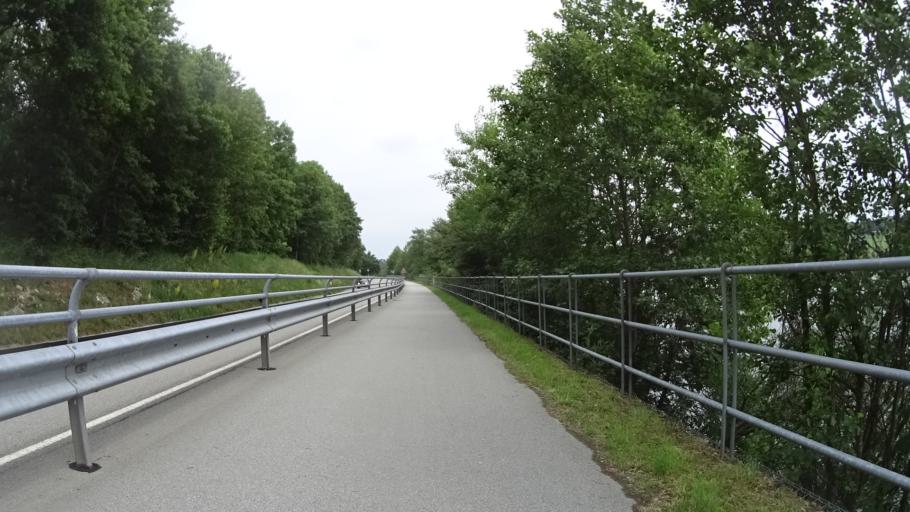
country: DE
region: Bavaria
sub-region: Lower Bavaria
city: Vilshofen
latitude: 48.6089
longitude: 13.2561
